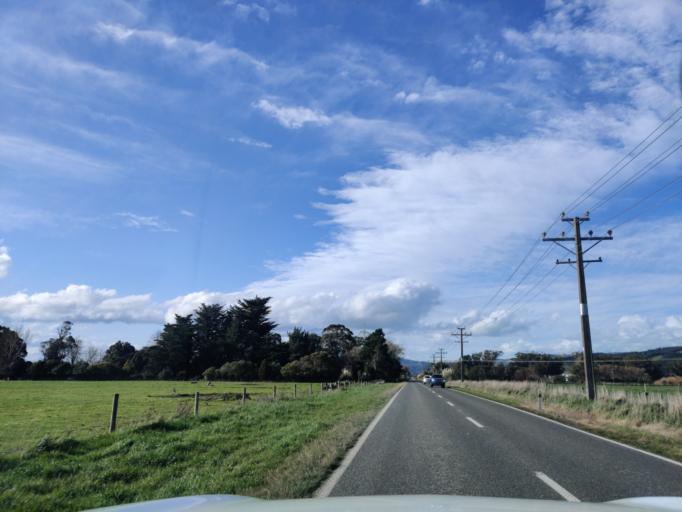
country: NZ
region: Manawatu-Wanganui
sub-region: Palmerston North City
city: Palmerston North
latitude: -40.3457
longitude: 175.7079
